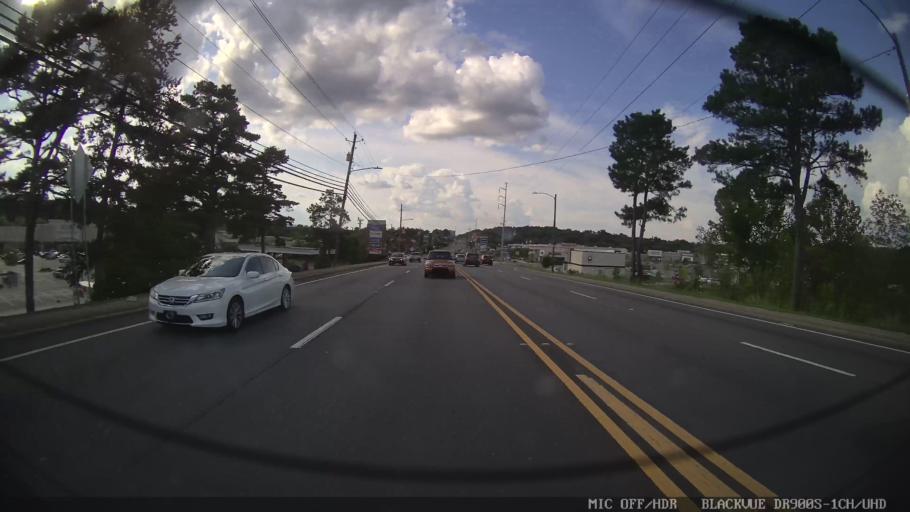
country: US
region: Georgia
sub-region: Floyd County
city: Rome
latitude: 34.2495
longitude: -85.1625
